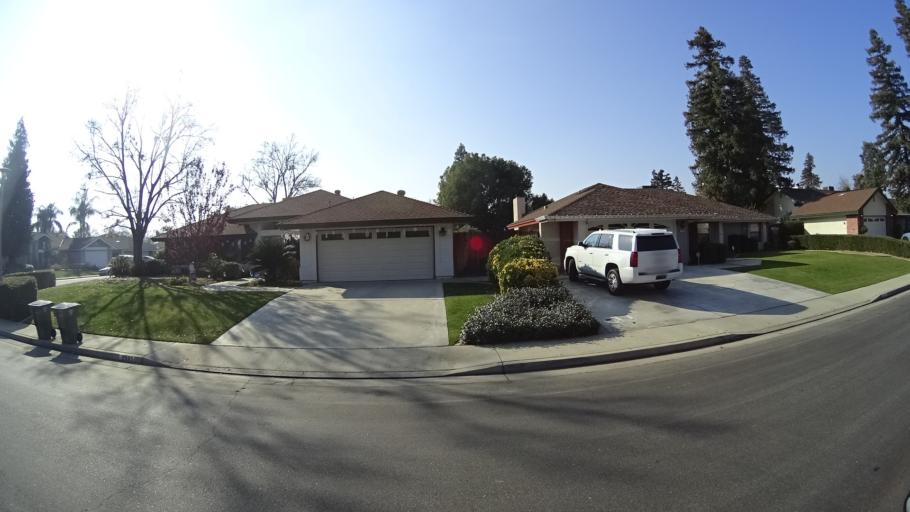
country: US
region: California
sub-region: Kern County
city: Greenacres
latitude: 35.3287
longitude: -119.1084
